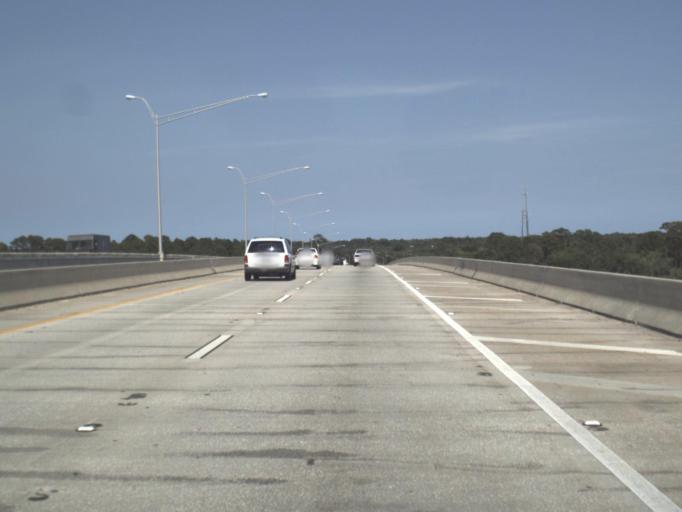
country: US
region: Florida
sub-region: Saint Johns County
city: Saint Augustine South
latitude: 29.8670
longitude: -81.3068
